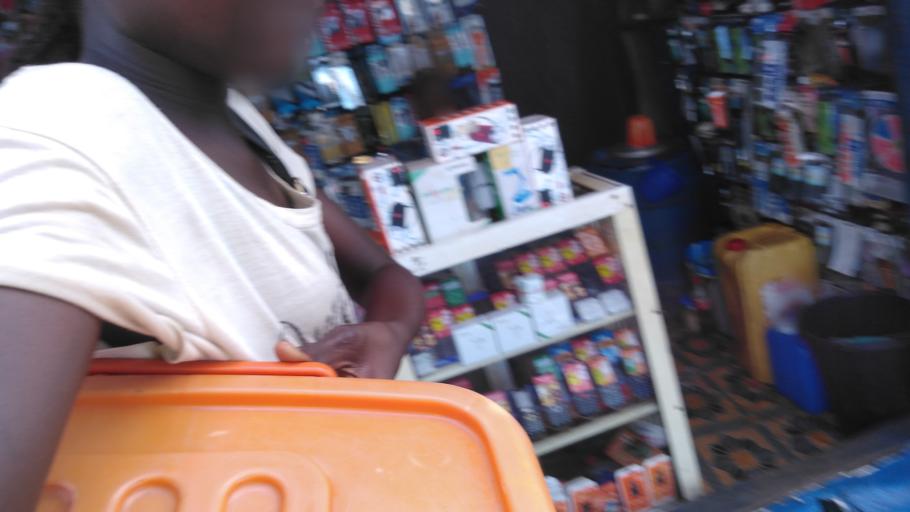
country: NG
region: Ondo
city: Igbekebo
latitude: 5.9206
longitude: 4.9672
